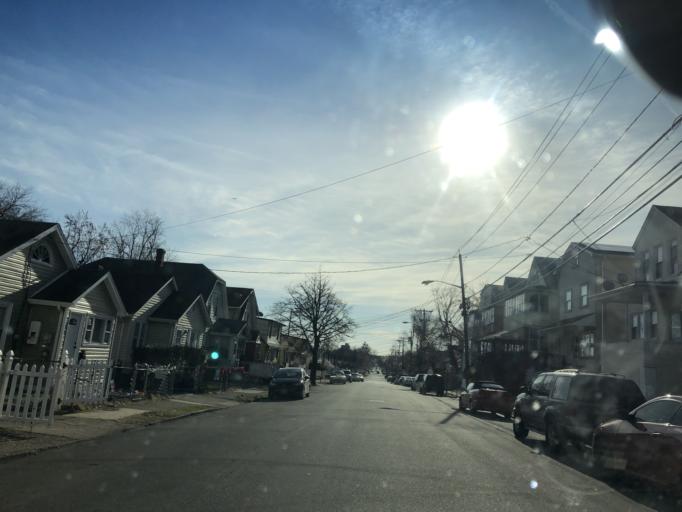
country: US
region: New Jersey
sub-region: Bergen County
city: Fair Lawn
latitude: 40.9317
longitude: -74.1446
